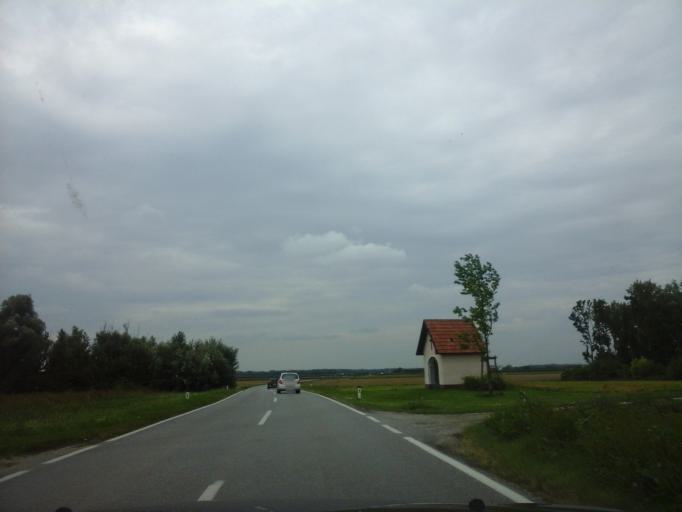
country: AT
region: Lower Austria
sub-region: Politischer Bezirk Ganserndorf
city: Orth an der Donau
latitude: 48.1598
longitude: 16.7443
